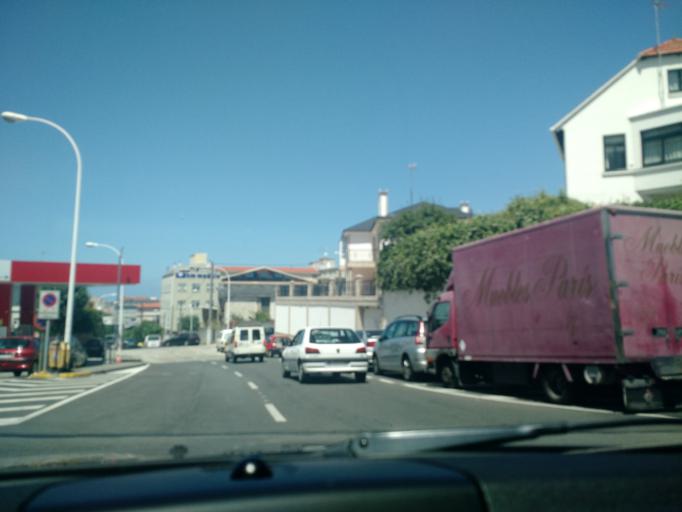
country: ES
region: Galicia
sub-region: Provincia da Coruna
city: A Coruna
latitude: 43.3653
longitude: -8.4187
